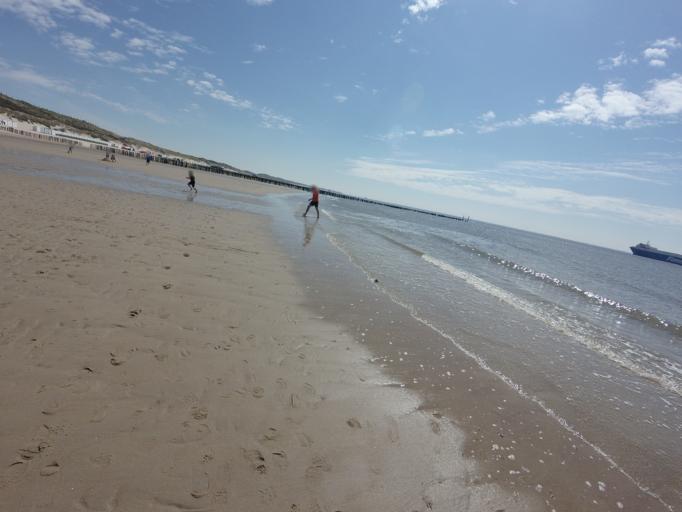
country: NL
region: Zeeland
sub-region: Gemeente Vlissingen
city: Vlissingen
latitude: 51.5078
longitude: 3.4623
